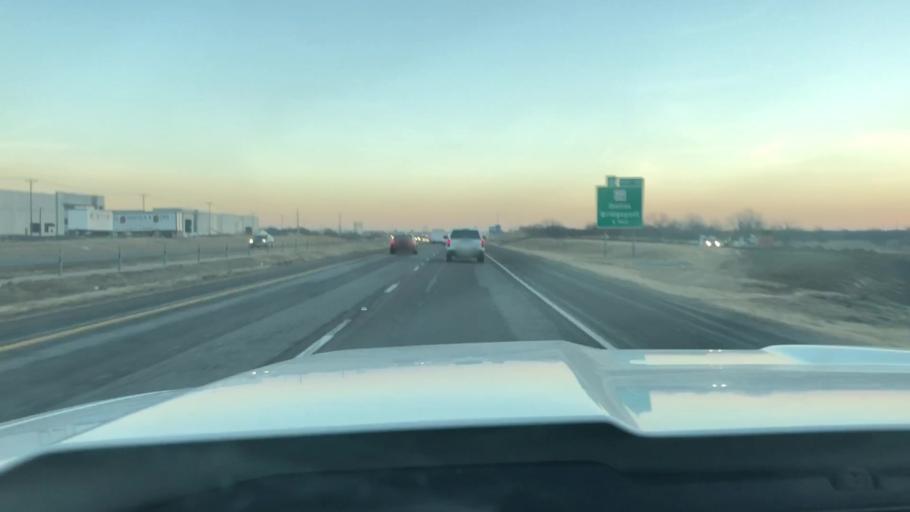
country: US
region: Texas
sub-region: Denton County
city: Roanoke
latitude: 33.0082
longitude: -97.2873
